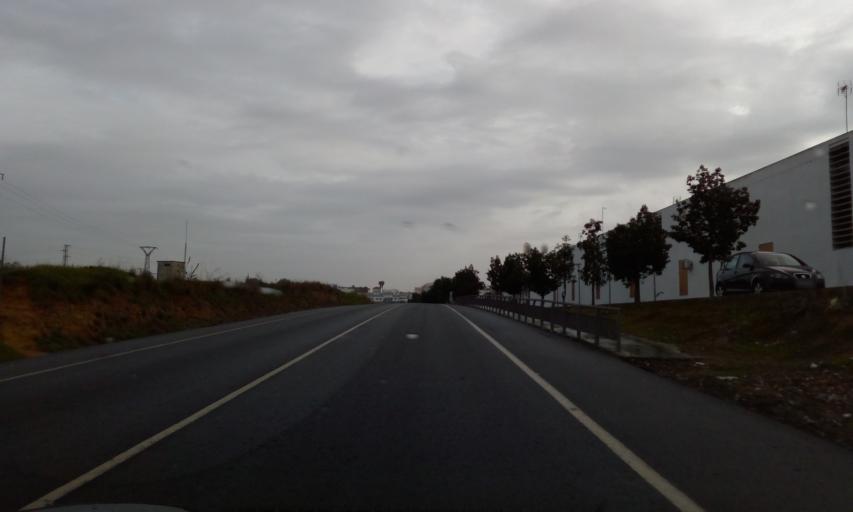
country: ES
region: Andalusia
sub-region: Provincia de Huelva
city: Cartaya
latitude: 37.2874
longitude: -7.1593
